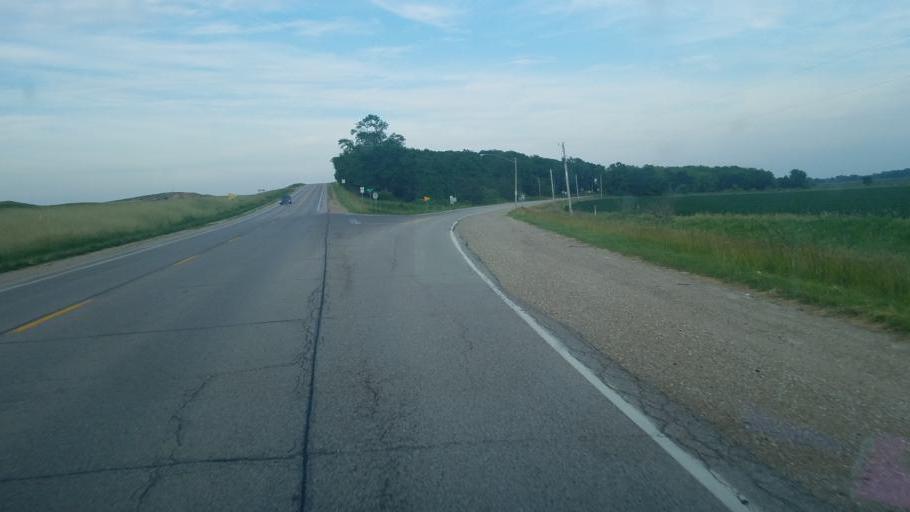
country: US
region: Iowa
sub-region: Tama County
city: Tama
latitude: 41.9638
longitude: -92.4578
